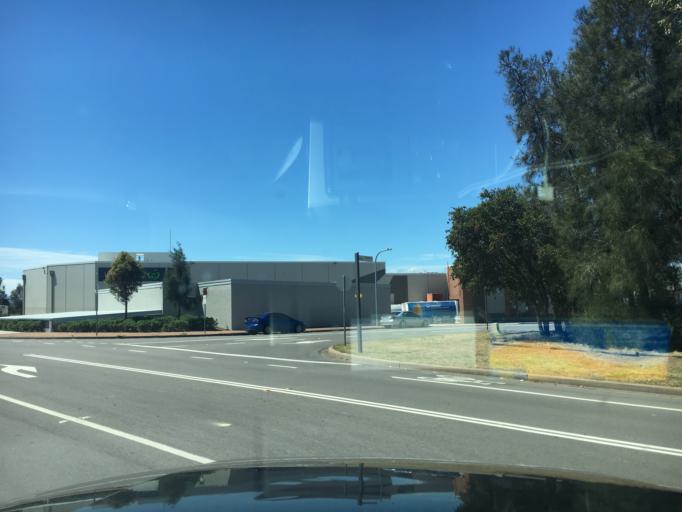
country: AU
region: New South Wales
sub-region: Singleton
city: Singleton
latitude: -32.5673
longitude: 151.1627
